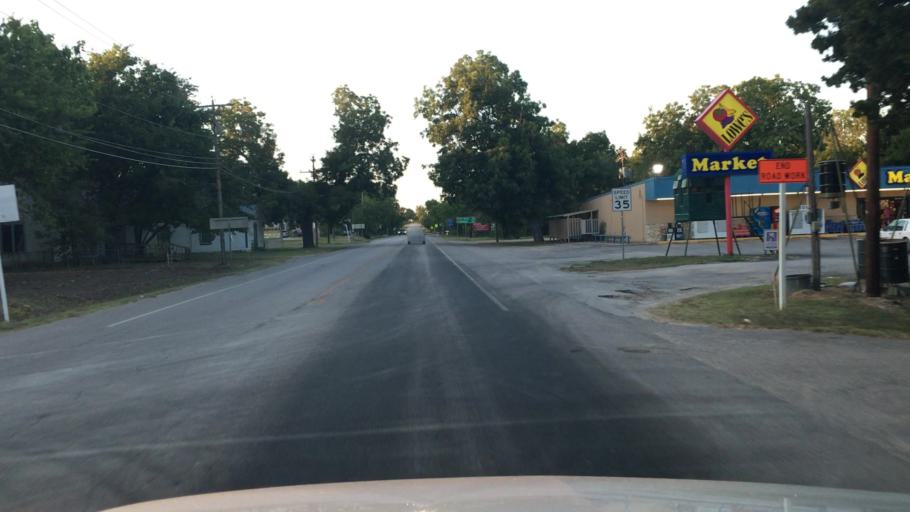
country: US
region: Texas
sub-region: Hamilton County
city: Hico
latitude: 31.9828
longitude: -98.0283
